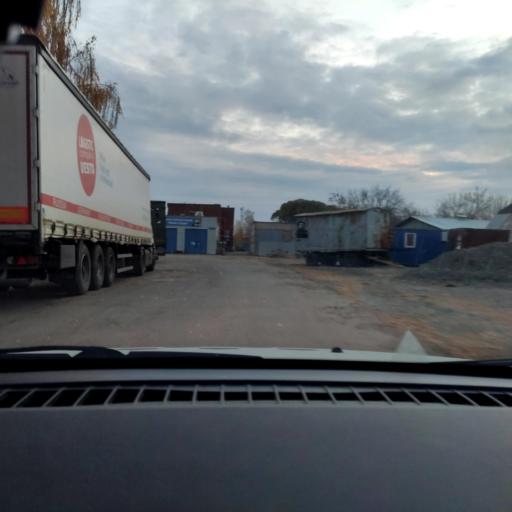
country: RU
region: Perm
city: Gamovo
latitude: 57.9052
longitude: 56.1706
